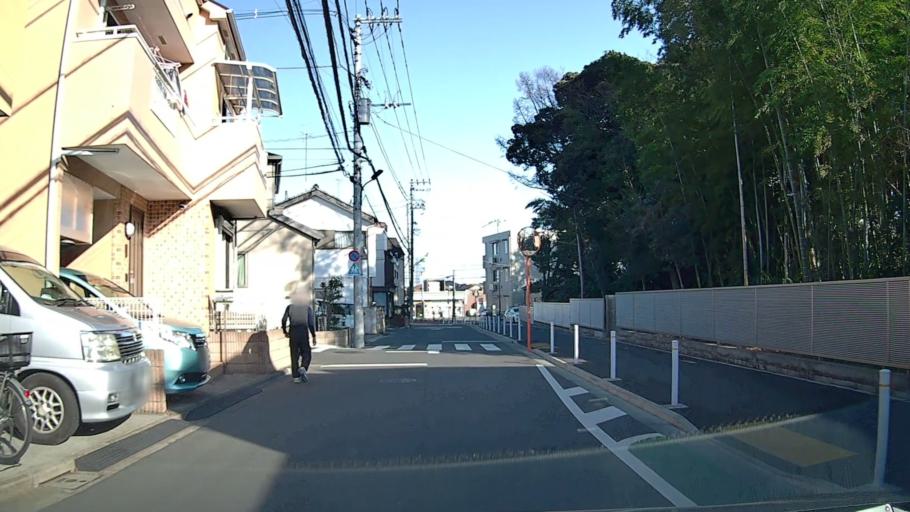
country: JP
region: Saitama
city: Wako
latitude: 35.7579
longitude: 139.6071
